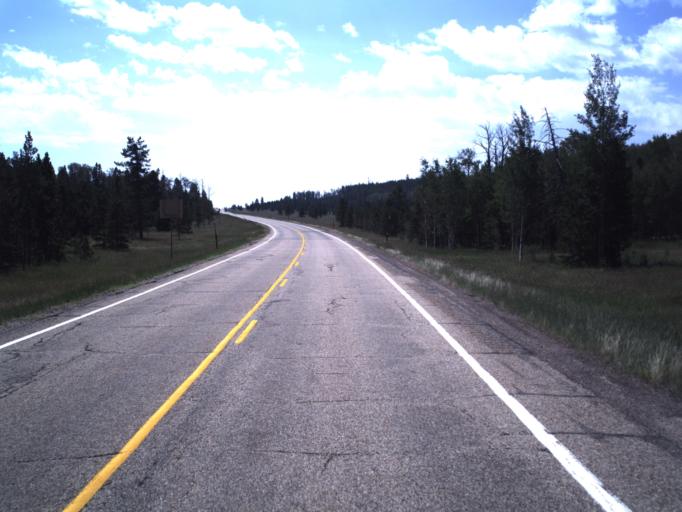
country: US
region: Utah
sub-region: Daggett County
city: Manila
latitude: 40.8081
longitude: -109.4676
